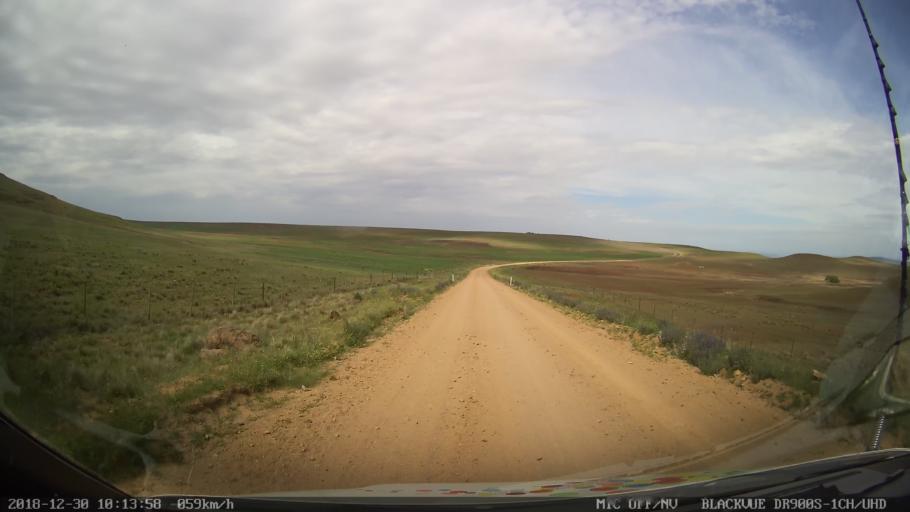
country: AU
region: New South Wales
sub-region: Snowy River
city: Berridale
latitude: -36.5400
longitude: 149.0604
